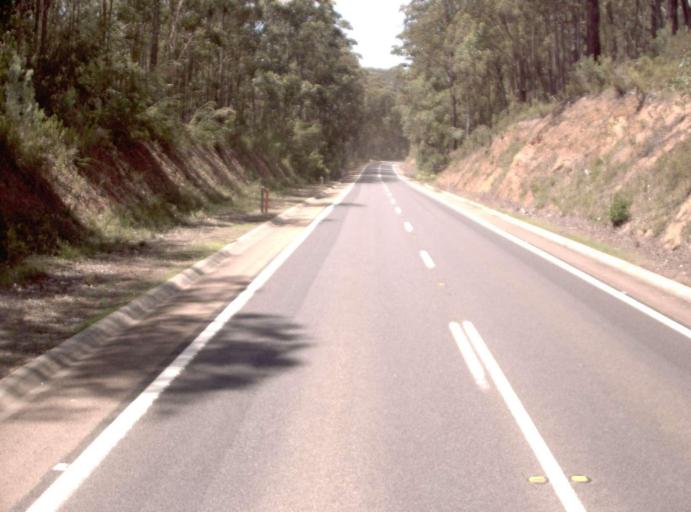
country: AU
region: New South Wales
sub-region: Bombala
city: Bombala
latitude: -37.5974
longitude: 148.9088
